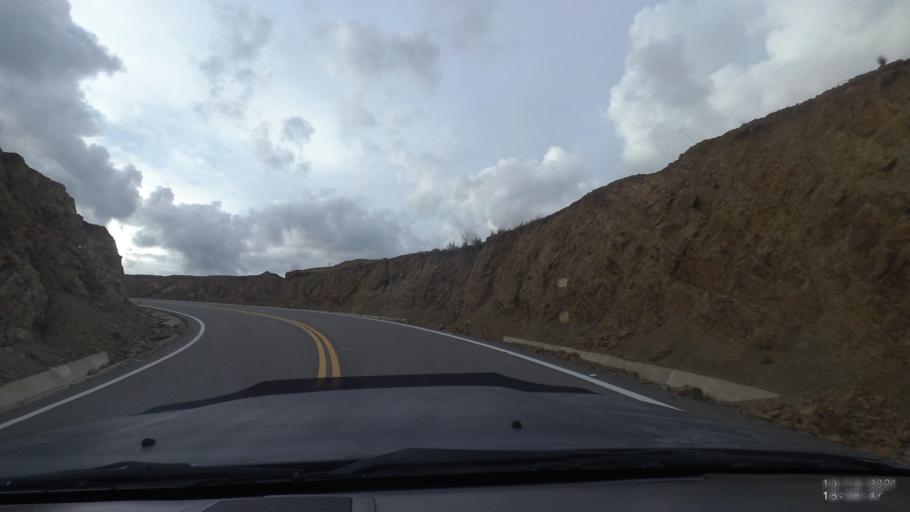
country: BO
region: Cochabamba
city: Tarata
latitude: -17.7900
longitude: -65.9464
